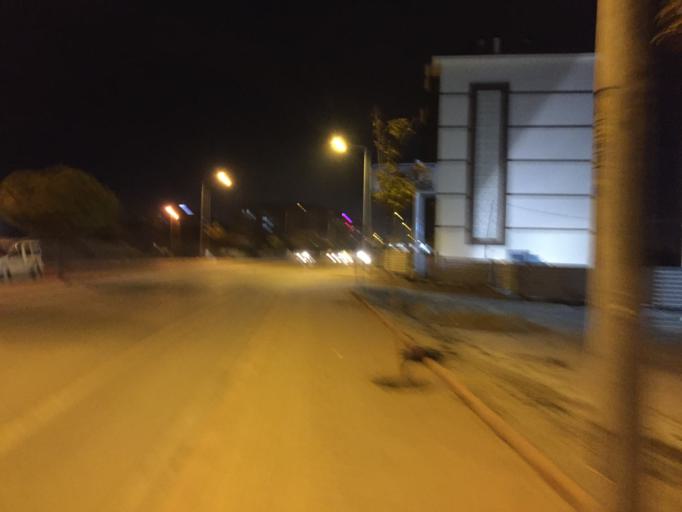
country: TR
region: Konya
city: Selcuklu
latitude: 37.8744
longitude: 32.5146
